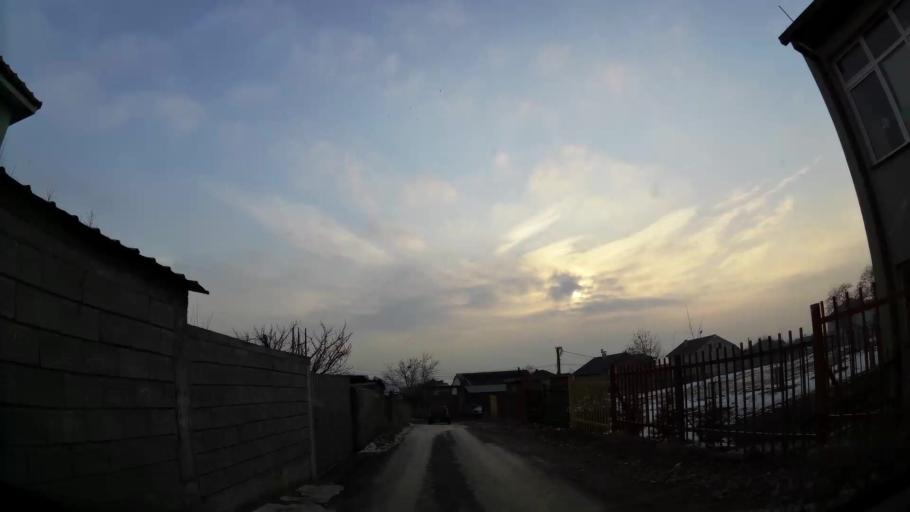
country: MK
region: Aracinovo
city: Arachinovo
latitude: 42.0237
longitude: 21.5608
